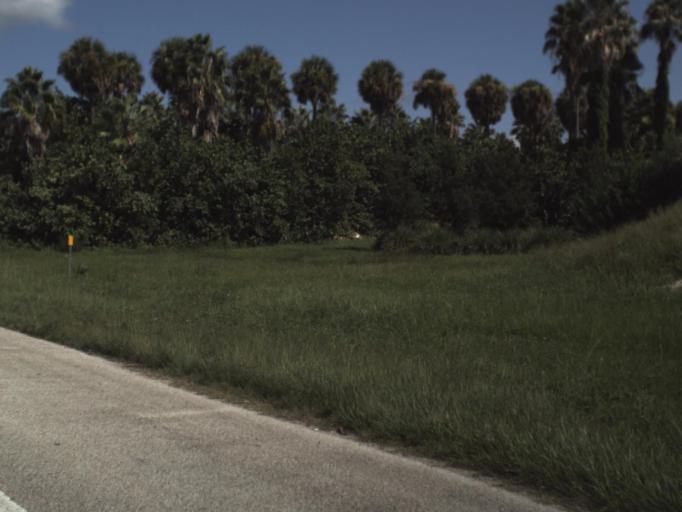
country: US
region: Florida
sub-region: Pinellas County
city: Feather Sound
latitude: 27.8784
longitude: -82.6581
